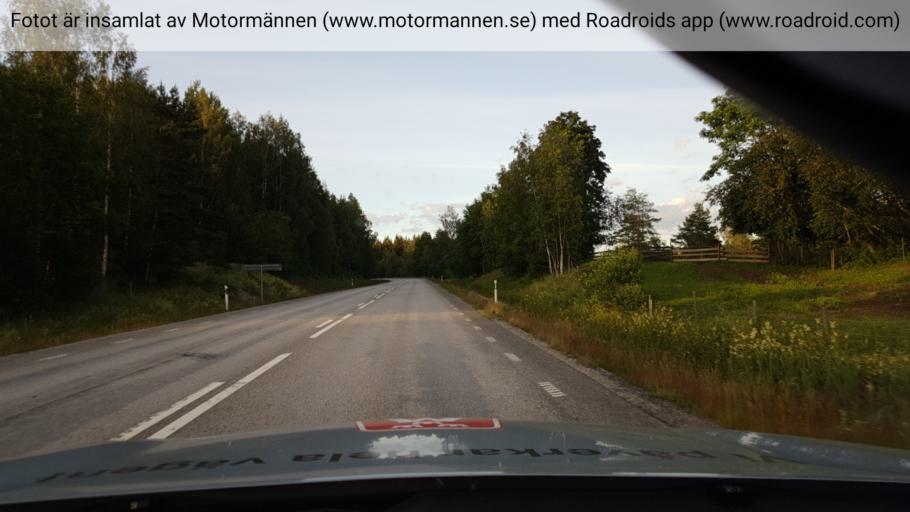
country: SE
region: OErebro
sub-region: Lindesbergs Kommun
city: Lindesberg
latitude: 59.6465
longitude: 15.2385
